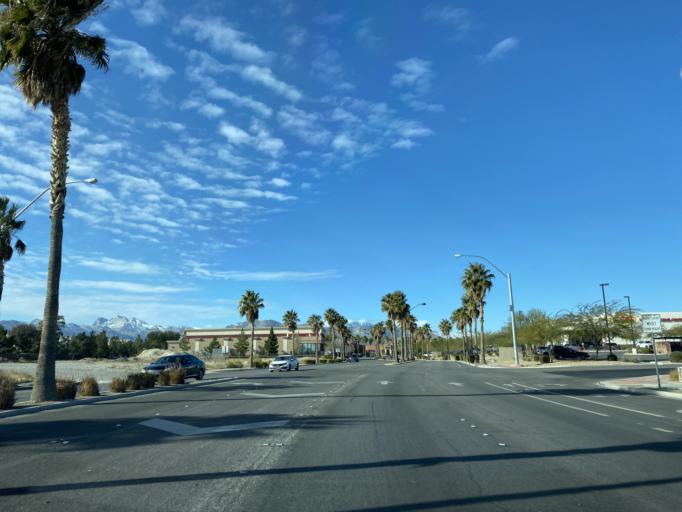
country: US
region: Nevada
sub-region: Clark County
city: Las Vegas
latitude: 36.2736
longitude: -115.2538
